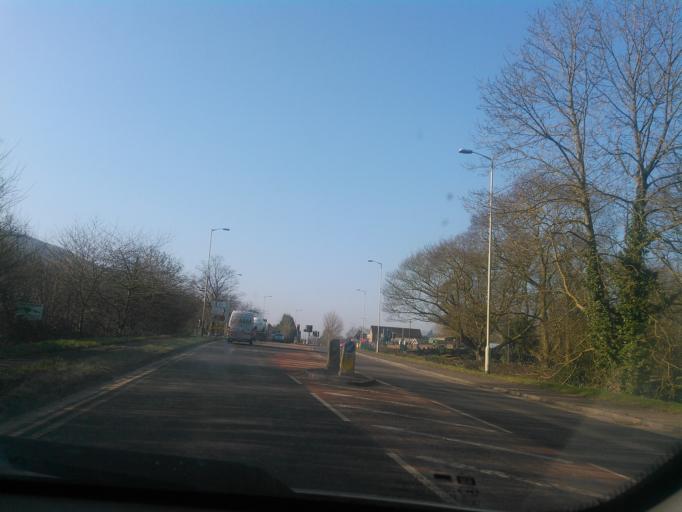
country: GB
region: England
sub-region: Shropshire
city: Church Stretton
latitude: 52.5385
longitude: -2.8002
